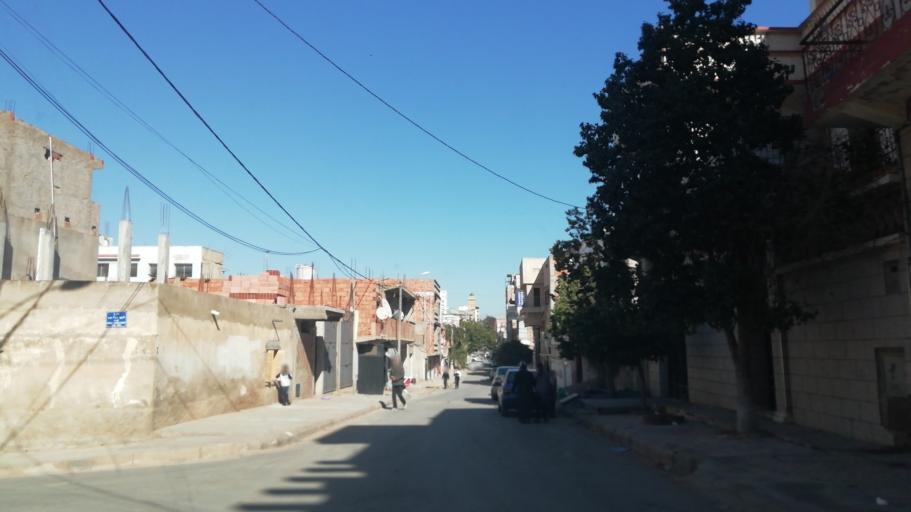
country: DZ
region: Oran
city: Bir el Djir
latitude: 35.7239
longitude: -0.5822
